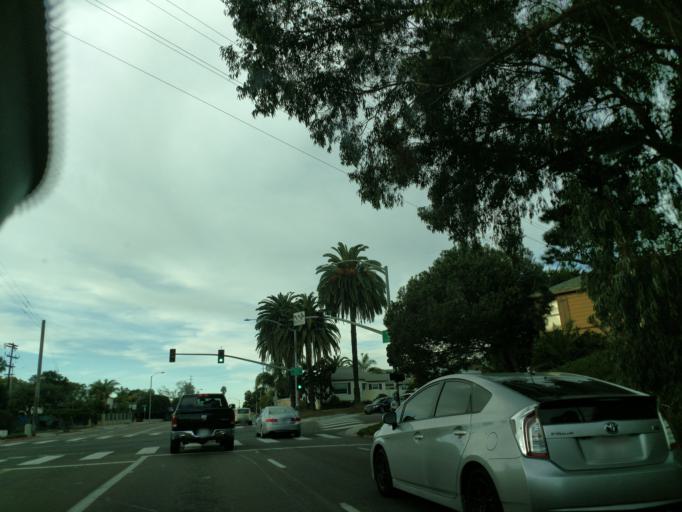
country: US
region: California
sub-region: San Diego County
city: Coronado
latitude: 32.7370
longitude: -117.2305
